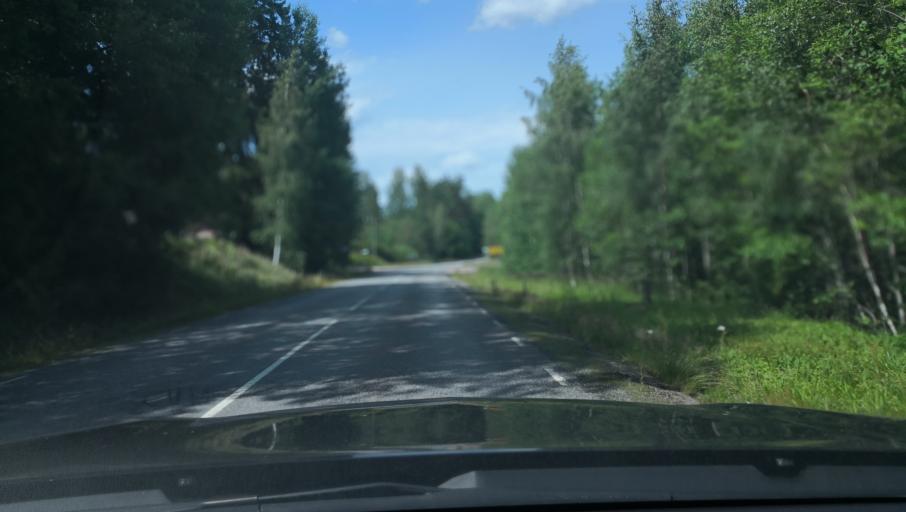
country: SE
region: Vaestmanland
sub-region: Surahammars Kommun
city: Ramnas
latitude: 59.7943
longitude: 16.1755
